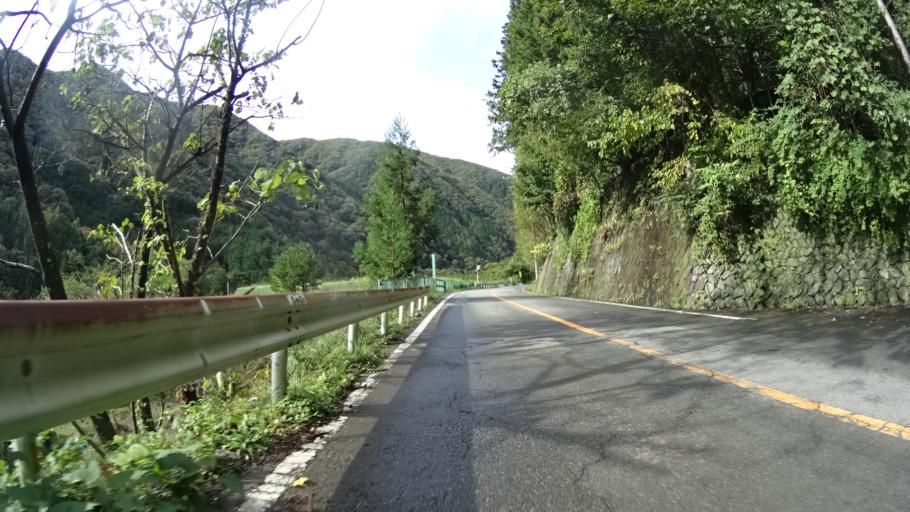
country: JP
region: Yamanashi
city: Otsuki
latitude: 35.7949
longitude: 138.9085
